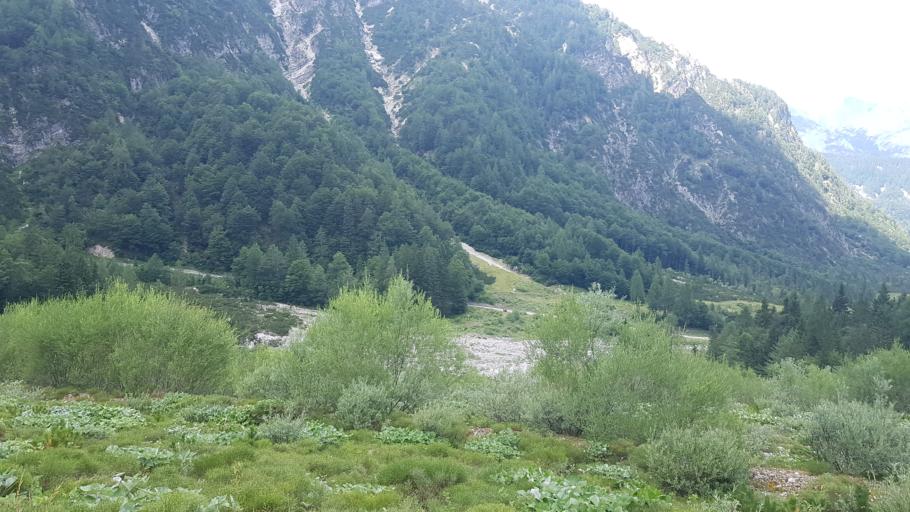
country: IT
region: Friuli Venezia Giulia
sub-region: Provincia di Udine
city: Pontebba
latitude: 46.4806
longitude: 13.2546
